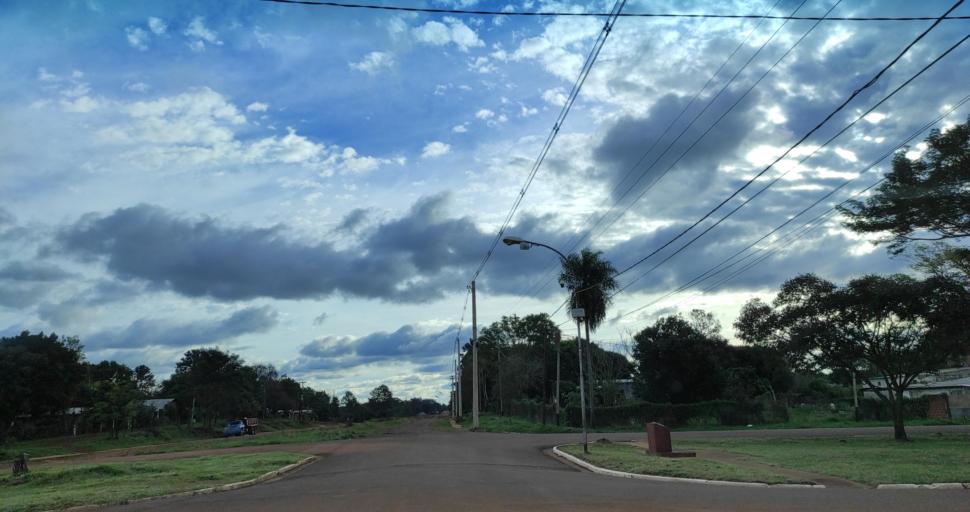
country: AR
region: Misiones
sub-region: Departamento de Candelaria
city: Candelaria
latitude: -27.4626
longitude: -55.7342
